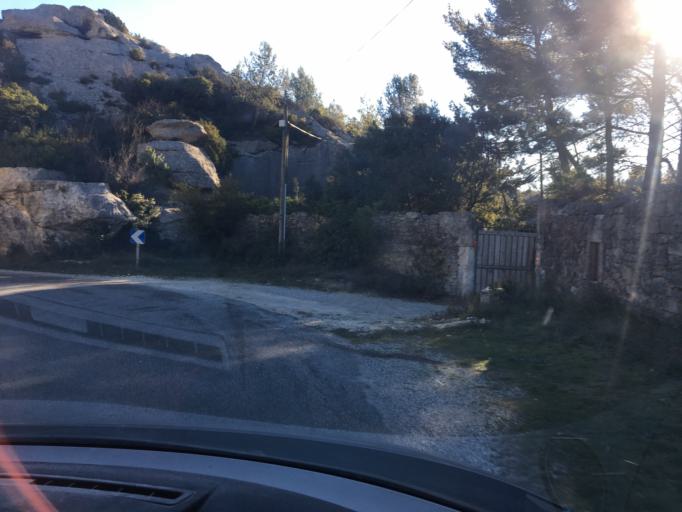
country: FR
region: Provence-Alpes-Cote d'Azur
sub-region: Departement des Bouches-du-Rhone
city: Maussane-les-Alpilles
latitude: 43.7506
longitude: 4.7913
